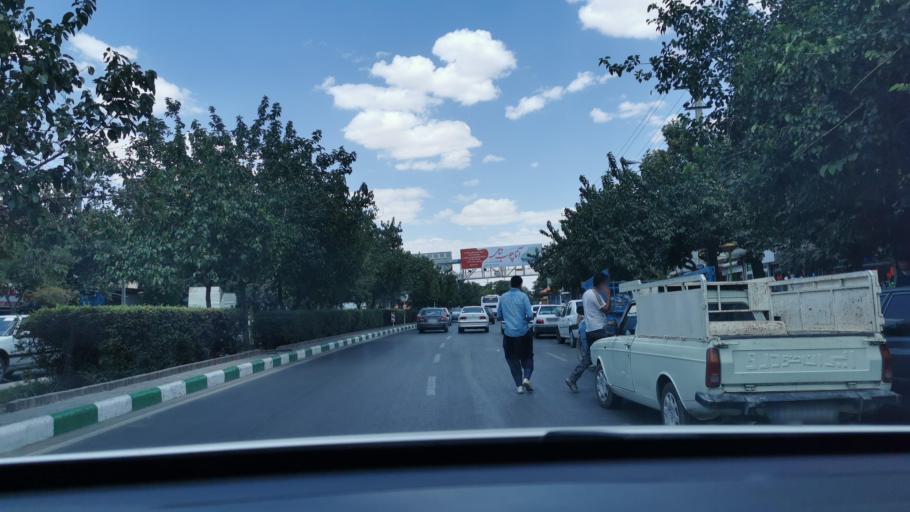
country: IR
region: Razavi Khorasan
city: Mashhad
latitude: 36.3408
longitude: 59.6249
